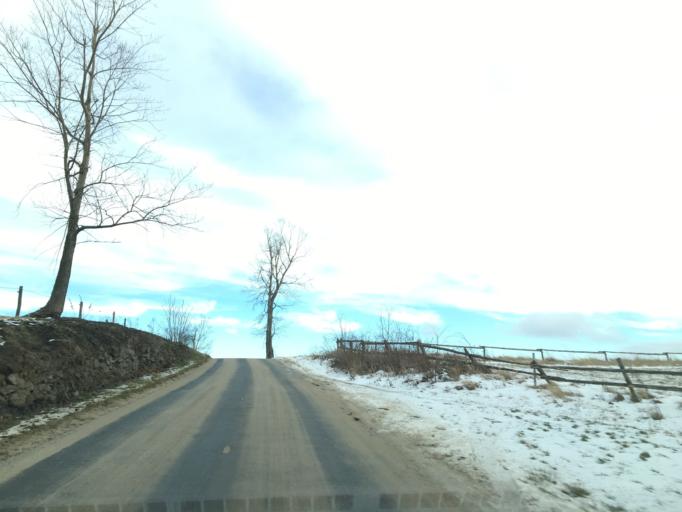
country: PL
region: Lower Silesian Voivodeship
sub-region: Powiat walbrzyski
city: Jedlina-Zdroj
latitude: 50.7360
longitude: 16.3790
